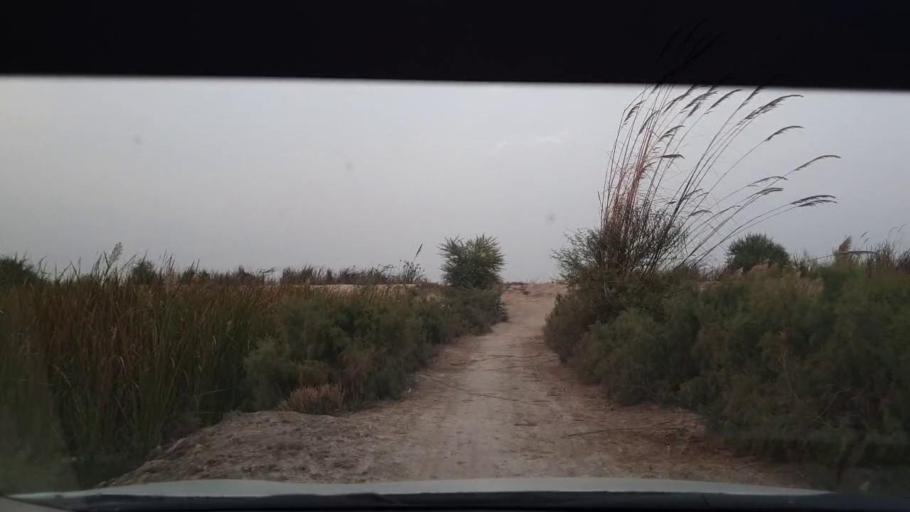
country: PK
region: Sindh
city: Berani
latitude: 25.8703
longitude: 68.7685
